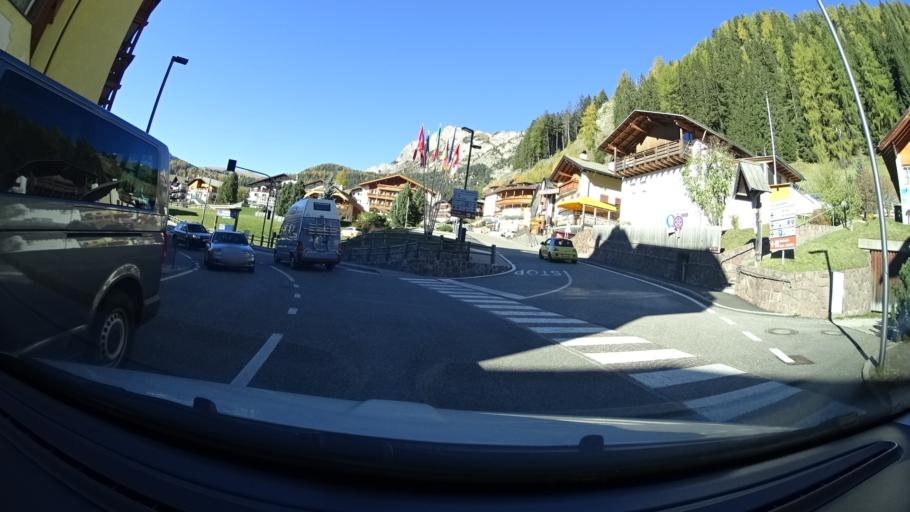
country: IT
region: Trentino-Alto Adige
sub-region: Bolzano
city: Selva
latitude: 46.5528
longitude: 11.7635
